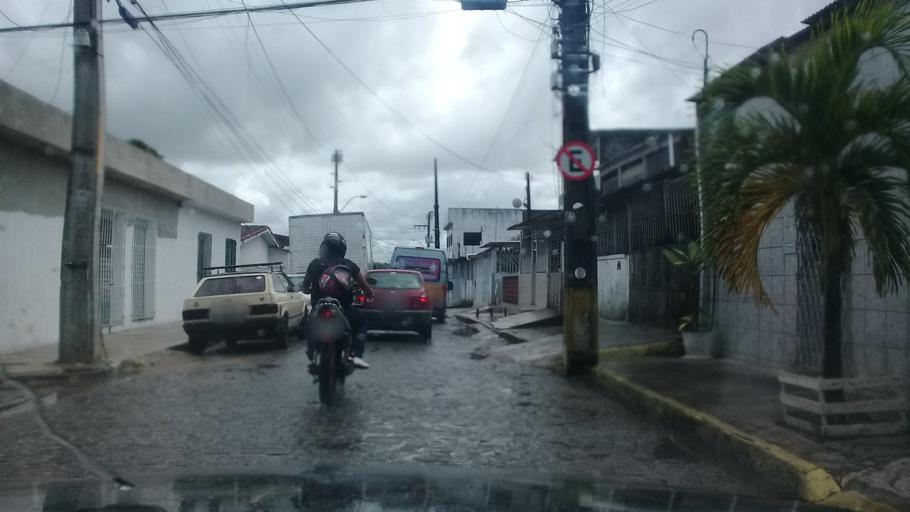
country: BR
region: Pernambuco
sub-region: Jaboatao Dos Guararapes
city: Jaboatao dos Guararapes
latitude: -8.1116
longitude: -34.9508
